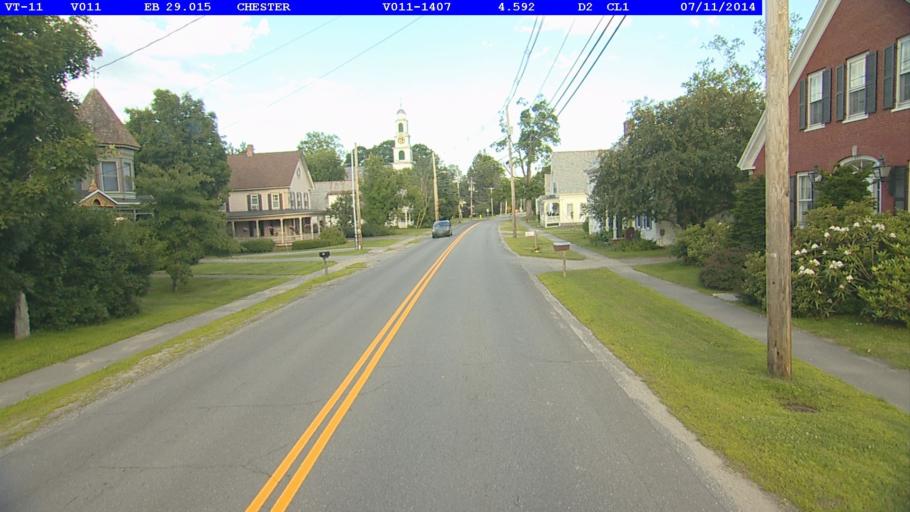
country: US
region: Vermont
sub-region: Windsor County
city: Chester
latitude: 43.2661
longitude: -72.6042
